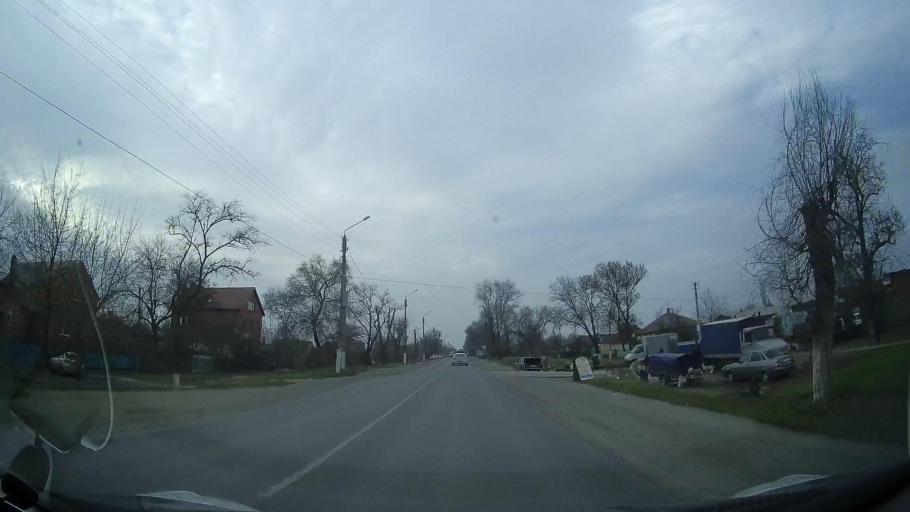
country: RU
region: Rostov
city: Ol'ginskaya
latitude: 47.1897
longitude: 39.9487
